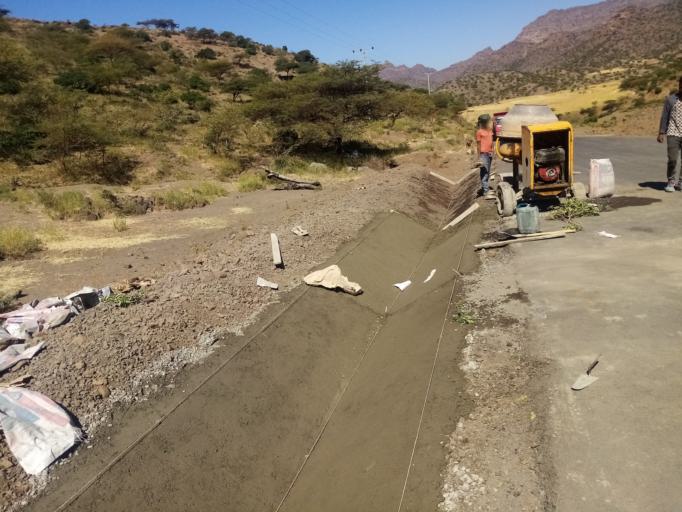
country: ET
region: Amhara
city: Lalibela
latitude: 12.2768
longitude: 39.0225
